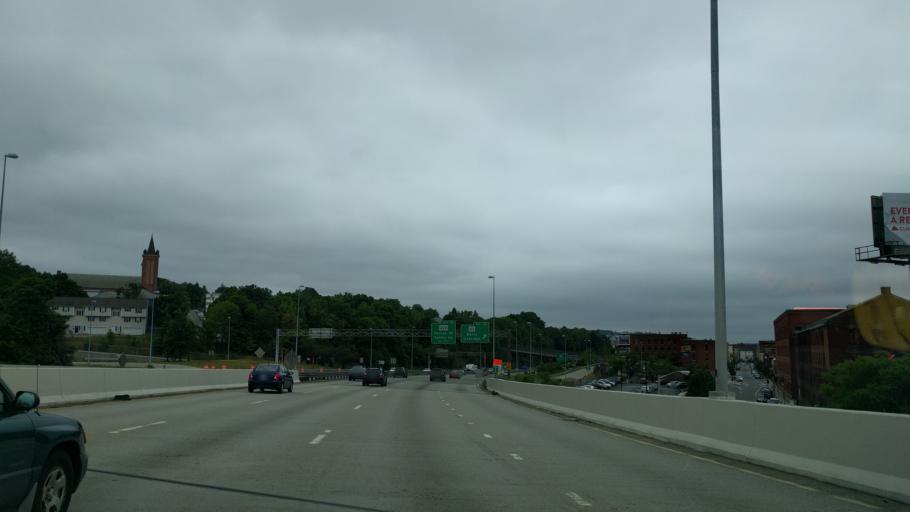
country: US
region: Massachusetts
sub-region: Worcester County
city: Worcester
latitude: 42.2590
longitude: -71.7936
